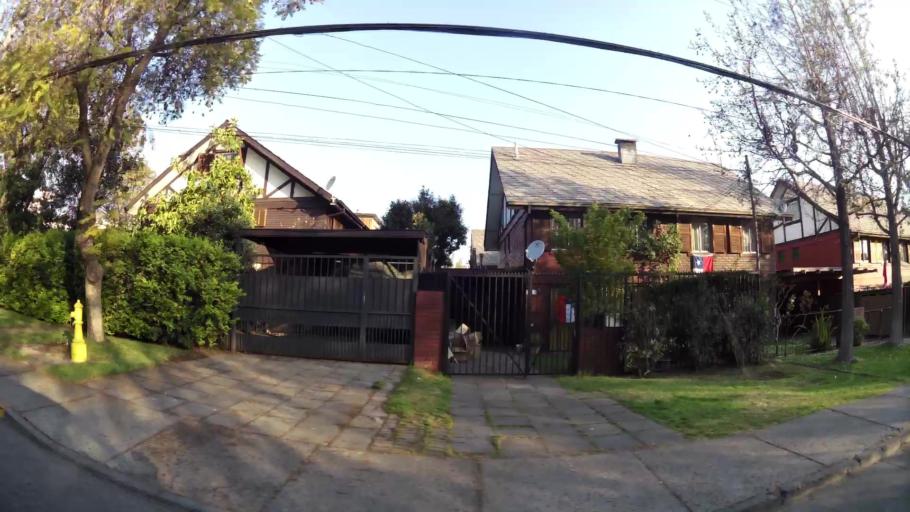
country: CL
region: Santiago Metropolitan
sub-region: Provincia de Santiago
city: Villa Presidente Frei, Nunoa, Santiago, Chile
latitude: -33.3923
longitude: -70.5482
